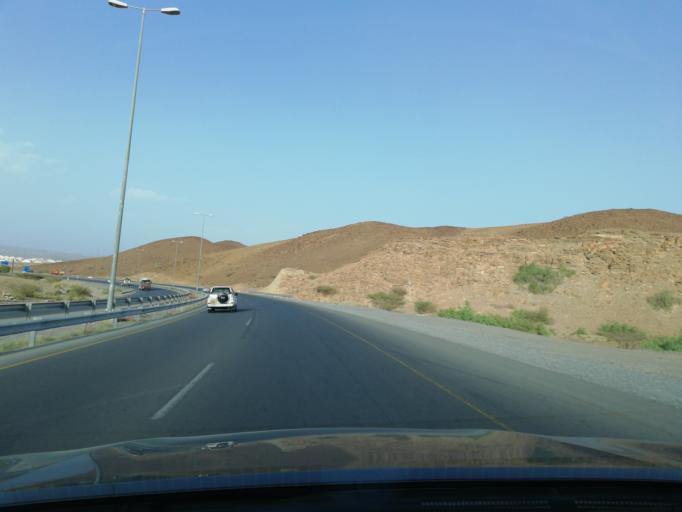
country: OM
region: Muhafazat ad Dakhiliyah
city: Izki
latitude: 22.8989
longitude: 57.7285
